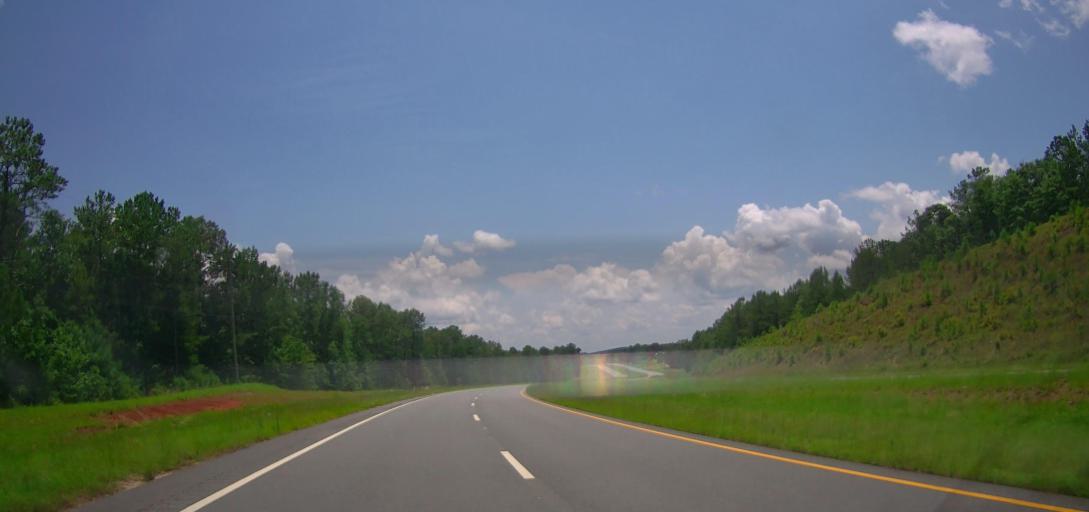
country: US
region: Georgia
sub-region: Upson County
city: Thomaston
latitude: 32.8167
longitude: -84.2882
